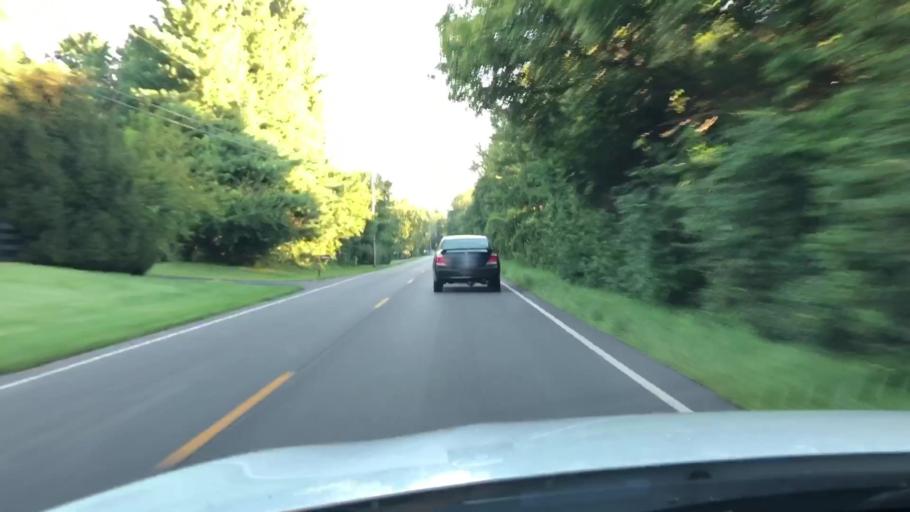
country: US
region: Kentucky
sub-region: Jefferson County
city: Middletown
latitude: 38.2166
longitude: -85.5076
